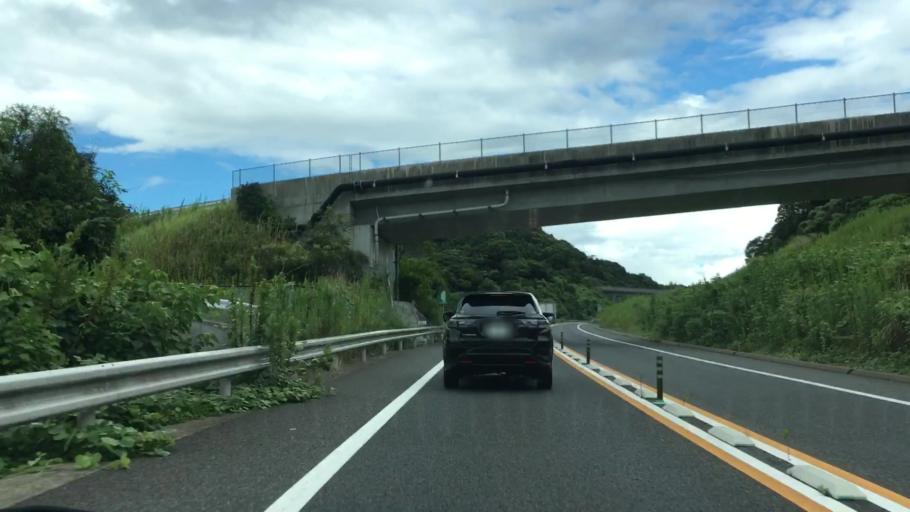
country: JP
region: Saga Prefecture
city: Karatsu
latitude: 33.3966
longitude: 129.9360
